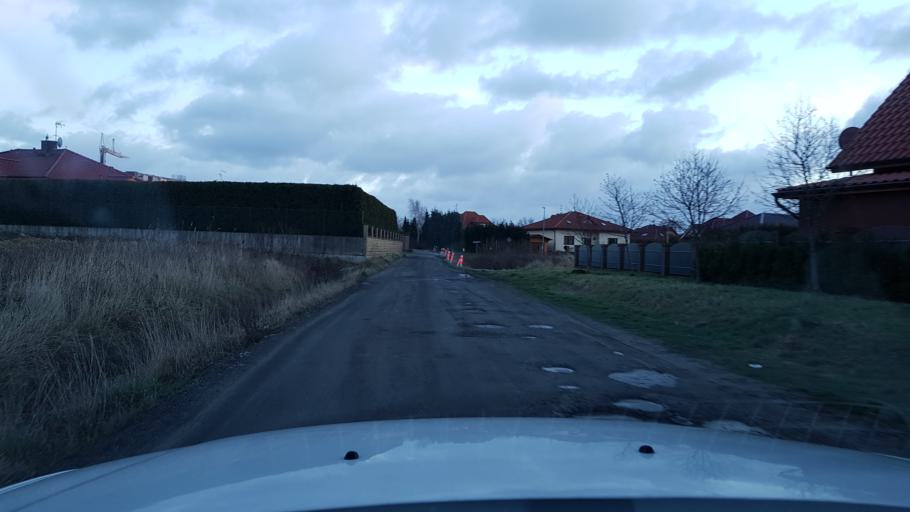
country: PL
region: West Pomeranian Voivodeship
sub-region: Powiat kolobrzeski
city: Kolobrzeg
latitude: 54.1516
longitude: 15.5564
